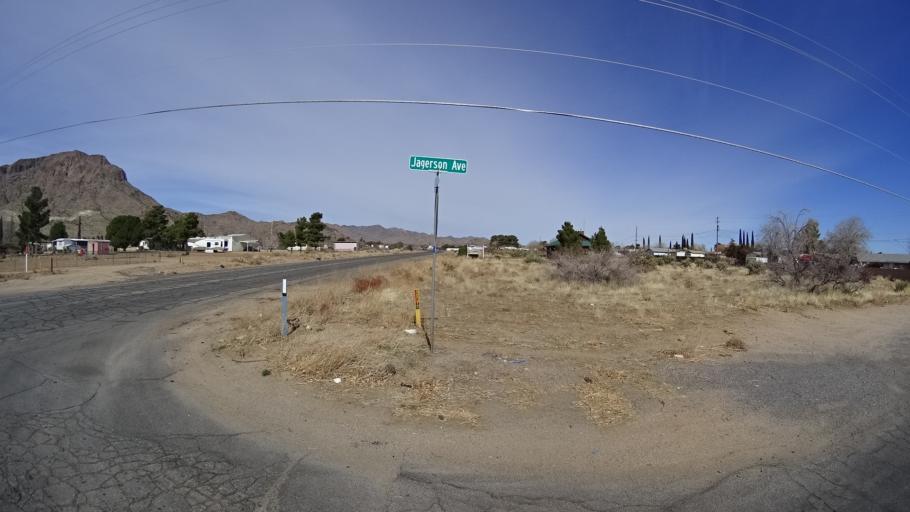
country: US
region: Arizona
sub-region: Mohave County
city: New Kingman-Butler
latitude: 35.2681
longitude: -114.0428
